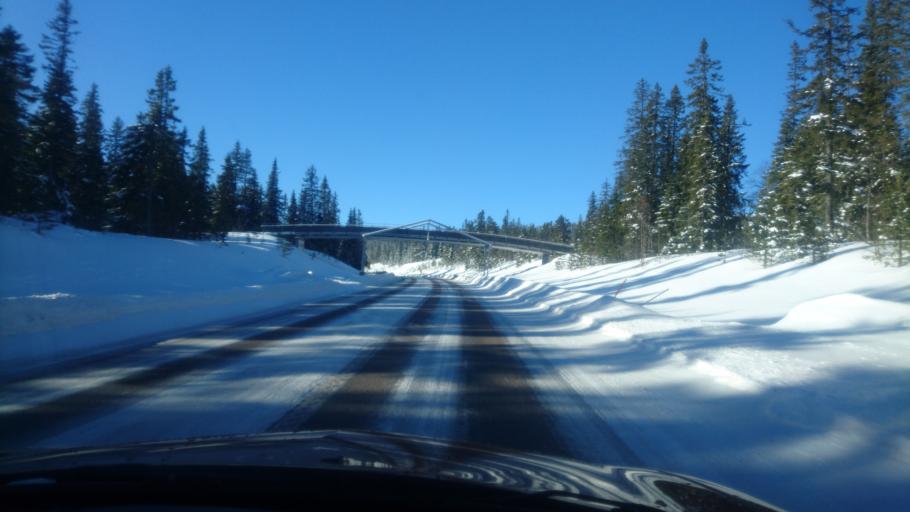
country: SE
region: Dalarna
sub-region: Malung-Saelens kommun
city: Malung
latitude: 61.1693
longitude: 13.1646
